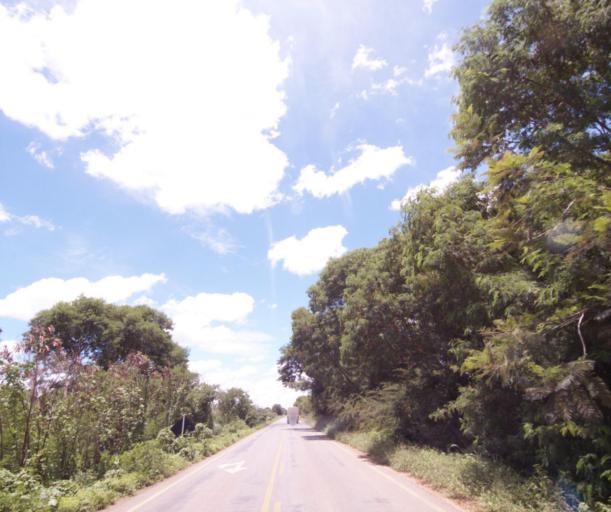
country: BR
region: Bahia
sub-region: Bom Jesus Da Lapa
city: Bom Jesus da Lapa
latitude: -13.2650
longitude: -43.5825
